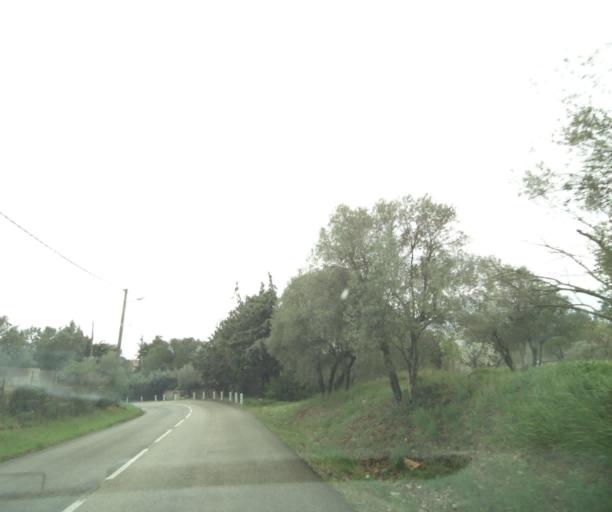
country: FR
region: Languedoc-Roussillon
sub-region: Departement de l'Herault
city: Pignan
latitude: 43.5888
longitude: 3.7529
